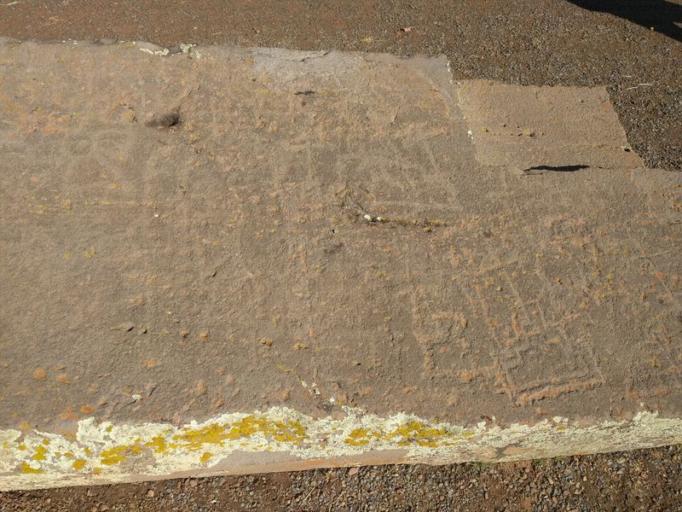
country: BO
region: La Paz
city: Tiahuanaco
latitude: -16.5556
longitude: -68.6703
